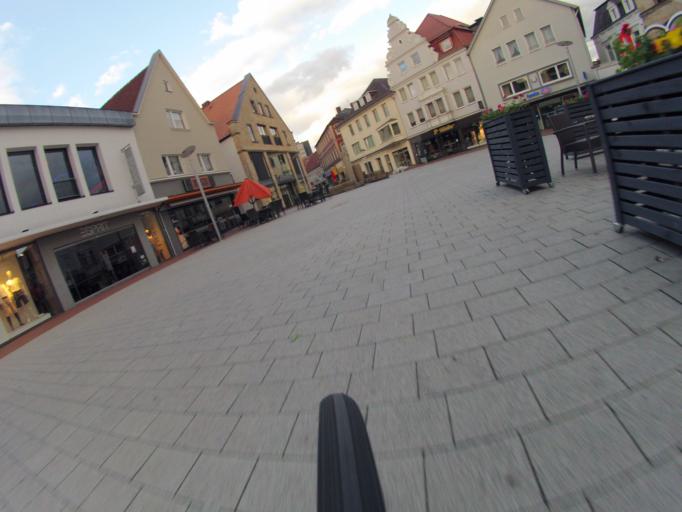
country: DE
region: North Rhine-Westphalia
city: Ibbenburen
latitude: 52.2763
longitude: 7.7157
